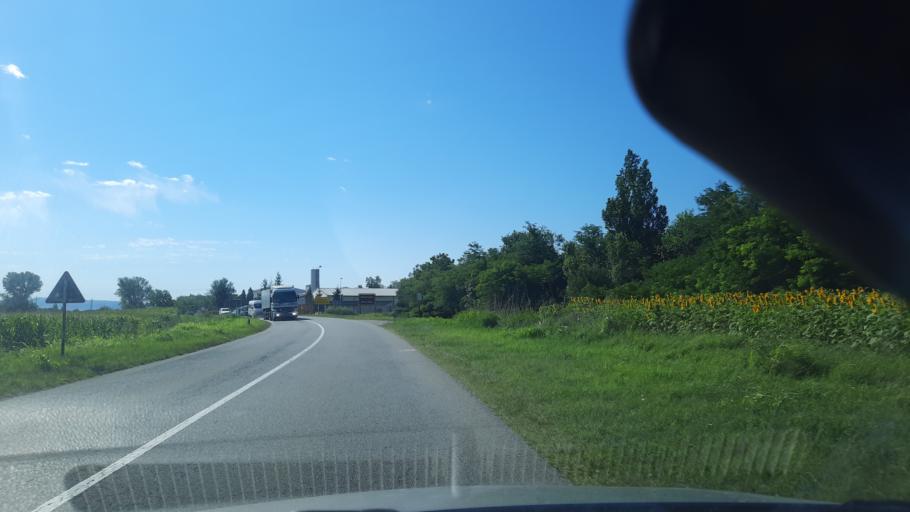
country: RS
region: Central Serbia
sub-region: Branicevski Okrug
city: Pozarevac
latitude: 44.7973
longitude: 21.1942
